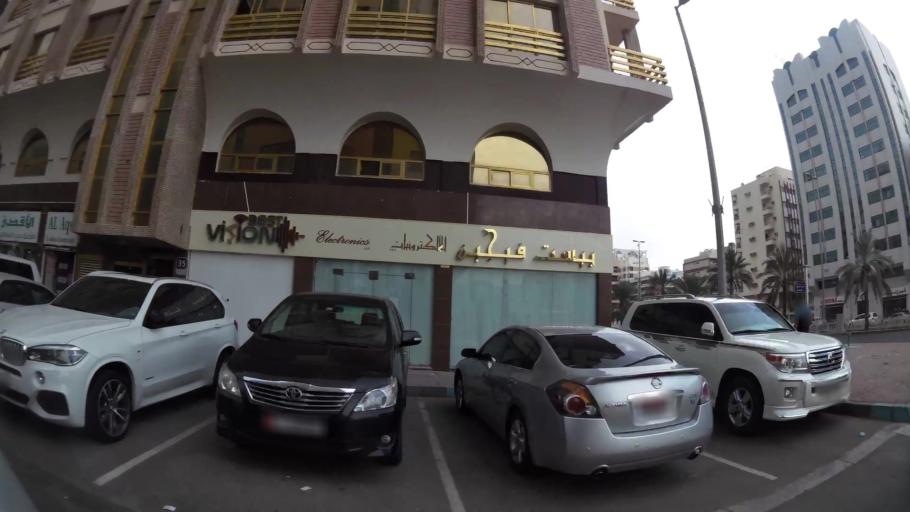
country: AE
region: Abu Dhabi
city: Abu Dhabi
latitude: 24.4901
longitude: 54.3796
